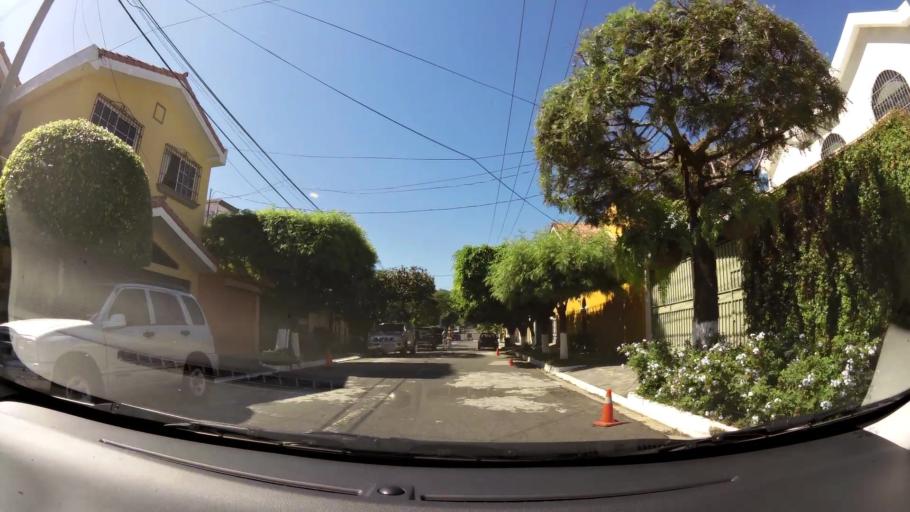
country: SV
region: La Libertad
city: Santa Tecla
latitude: 13.6662
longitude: -89.2798
